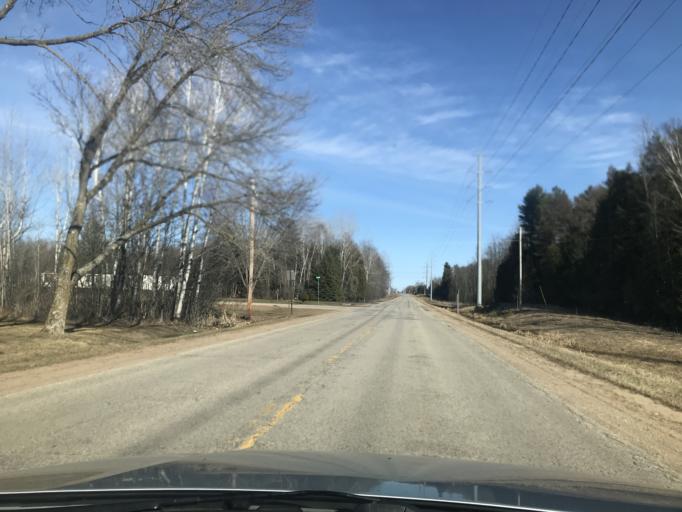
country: US
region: Wisconsin
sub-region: Marinette County
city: Marinette
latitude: 45.1449
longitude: -87.6445
